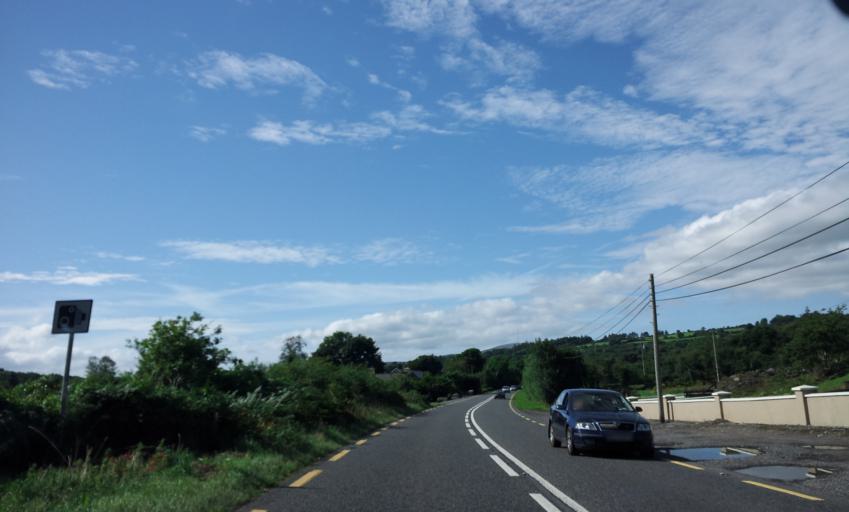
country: IE
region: Munster
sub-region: County Cork
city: Macroom
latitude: 51.9115
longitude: -9.0501
